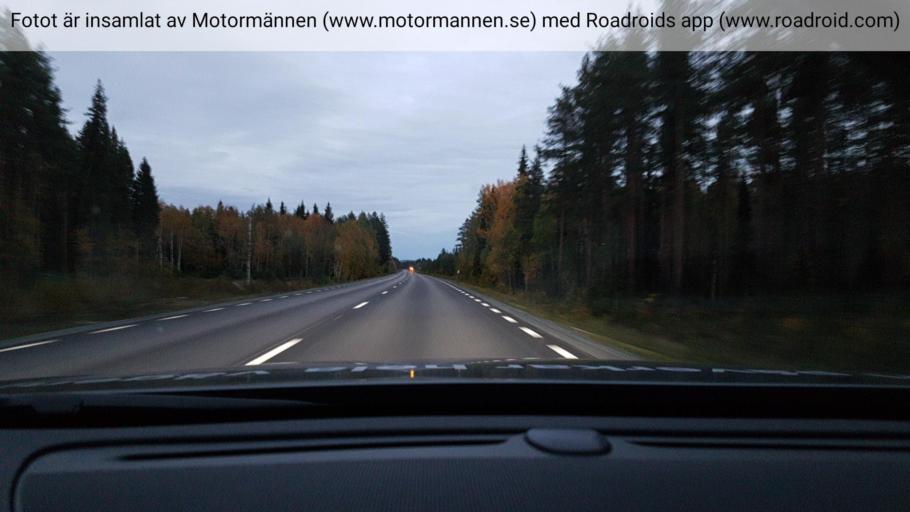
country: SE
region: Norrbotten
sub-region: Alvsbyns Kommun
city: AElvsbyn
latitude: 65.7556
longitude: 20.8928
